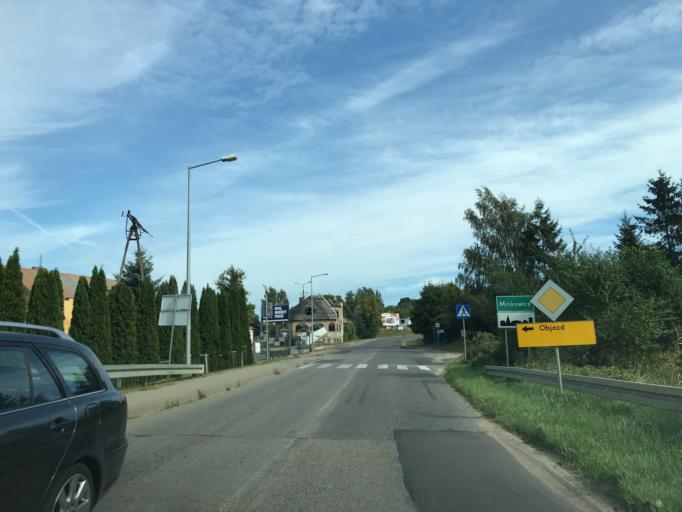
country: PL
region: Pomeranian Voivodeship
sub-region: Powiat pucki
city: Krokowa
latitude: 54.7817
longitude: 18.1695
